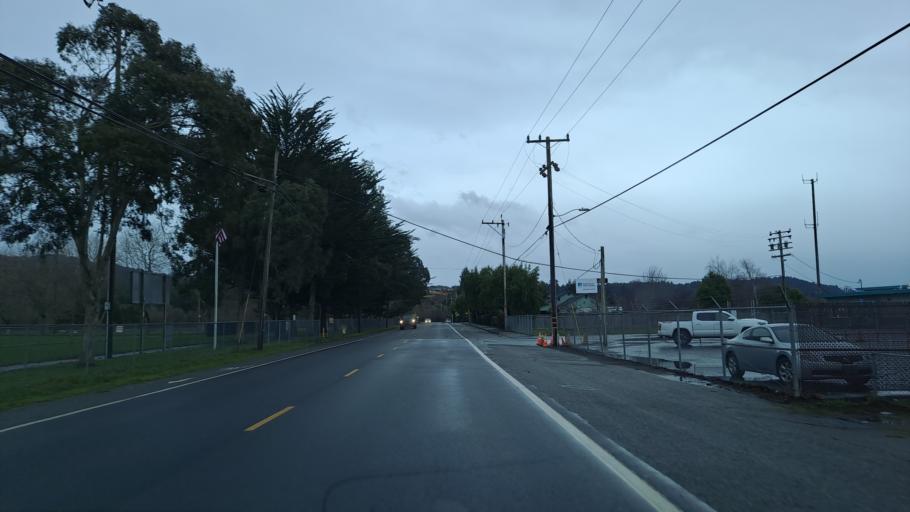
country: US
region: California
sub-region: Humboldt County
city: Fortuna
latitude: 40.5918
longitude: -124.1380
